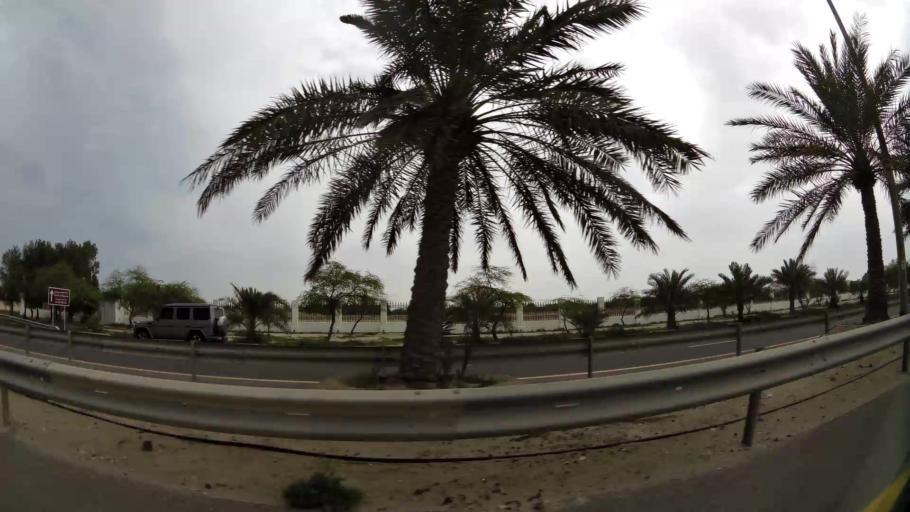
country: BH
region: Central Governorate
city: Dar Kulayb
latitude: 26.0675
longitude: 50.5232
